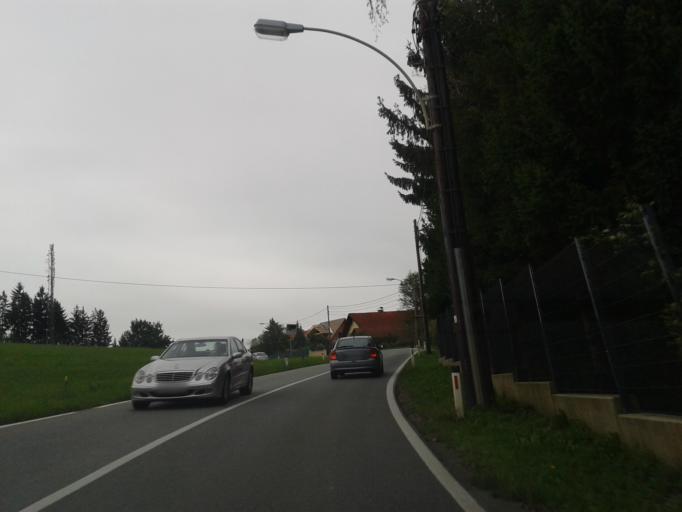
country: AT
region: Styria
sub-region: Graz Stadt
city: Mariatrost
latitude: 47.0825
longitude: 15.4784
